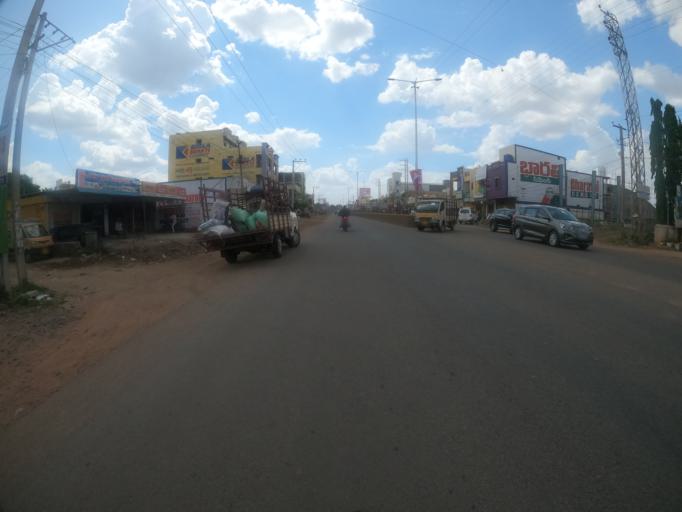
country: IN
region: Telangana
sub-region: Rangareddi
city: Sriramnagar
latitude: 17.3094
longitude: 78.1423
